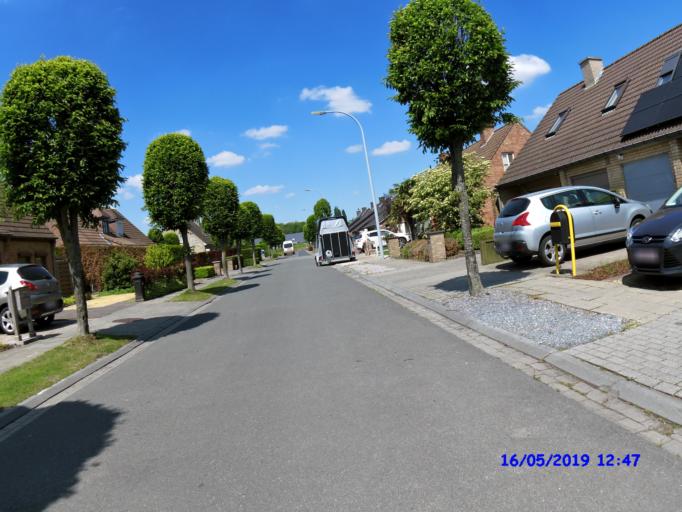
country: BE
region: Flanders
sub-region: Provincie West-Vlaanderen
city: Harelbeke
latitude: 50.8528
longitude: 3.2996
